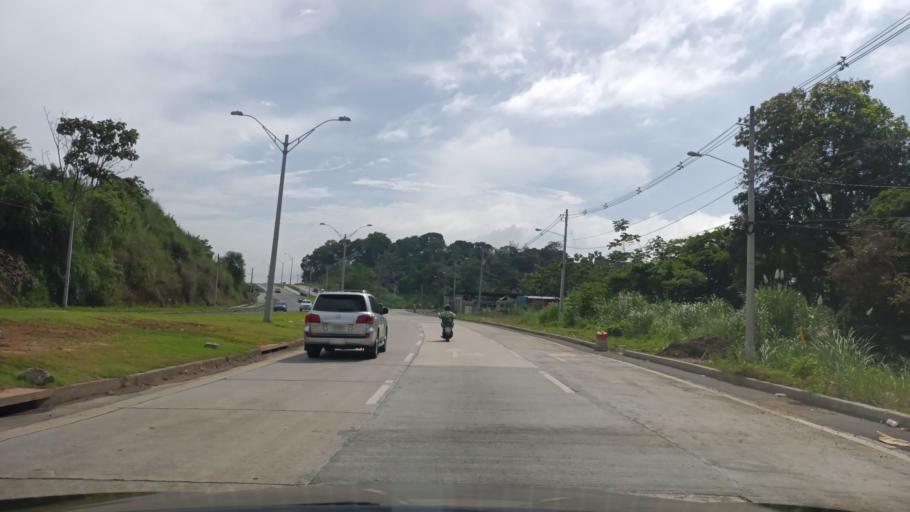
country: PA
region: Panama
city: Las Cumbres
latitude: 9.0996
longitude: -79.5148
